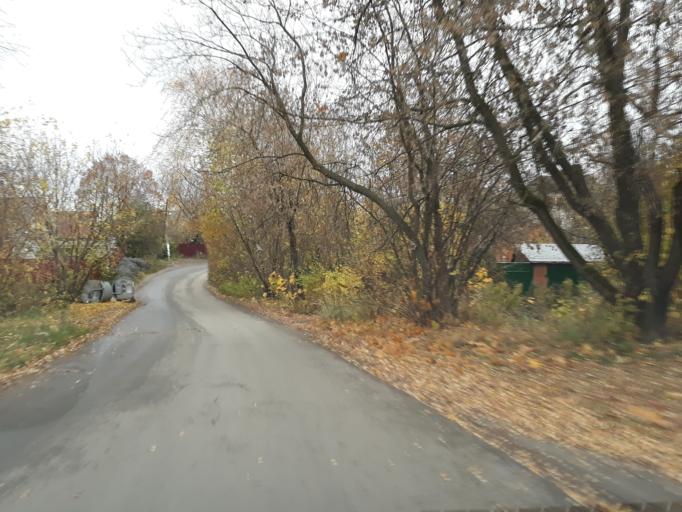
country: RU
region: Nizjnij Novgorod
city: Nizhniy Novgorod
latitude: 56.2535
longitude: 43.9758
